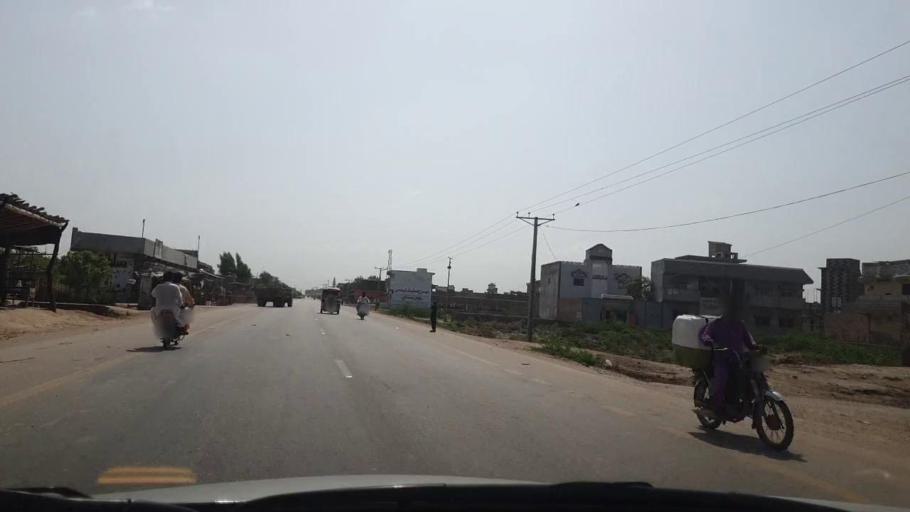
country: PK
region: Sindh
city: Matli
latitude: 25.0380
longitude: 68.6490
